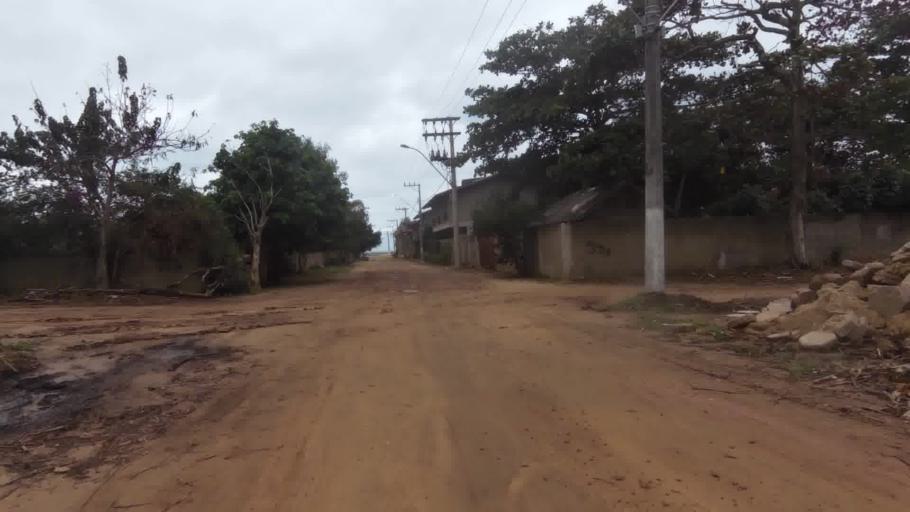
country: BR
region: Espirito Santo
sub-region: Marataizes
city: Marataizes
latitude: -21.0573
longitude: -40.8354
